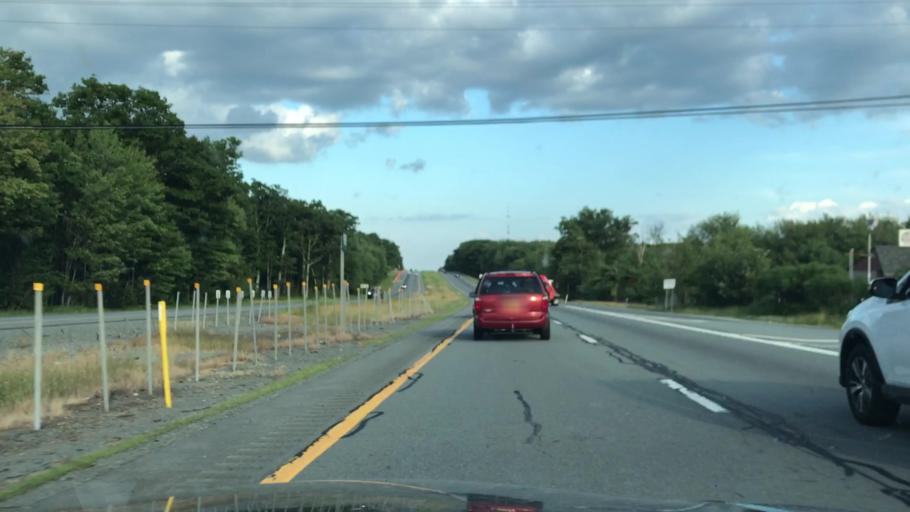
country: US
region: New York
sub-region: Sullivan County
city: Rock Hill
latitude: 41.6066
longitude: -74.5650
